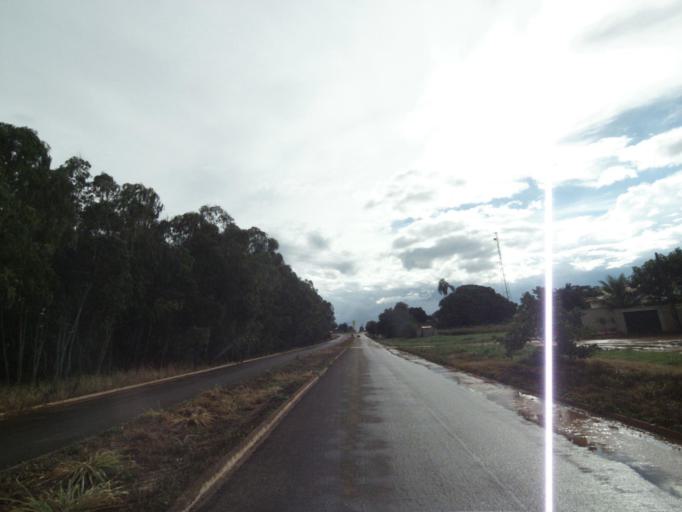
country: BR
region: Goias
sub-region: Itaberai
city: Itaberai
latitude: -15.9231
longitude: -49.6033
